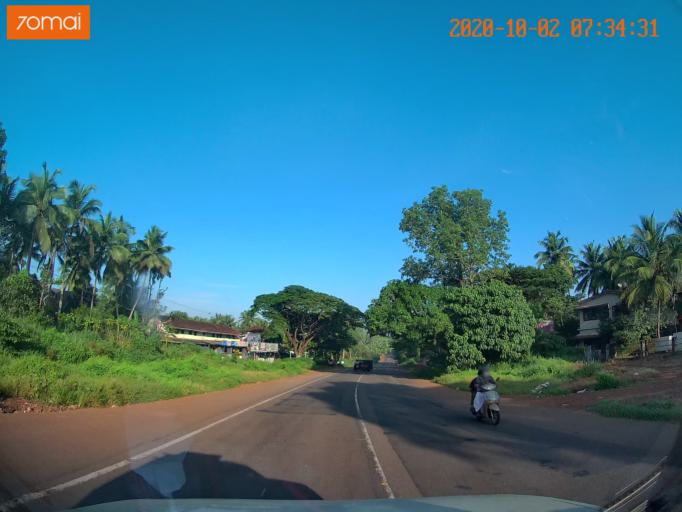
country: IN
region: Kerala
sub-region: Malappuram
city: Pariyapuram
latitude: 11.0635
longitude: 75.9289
